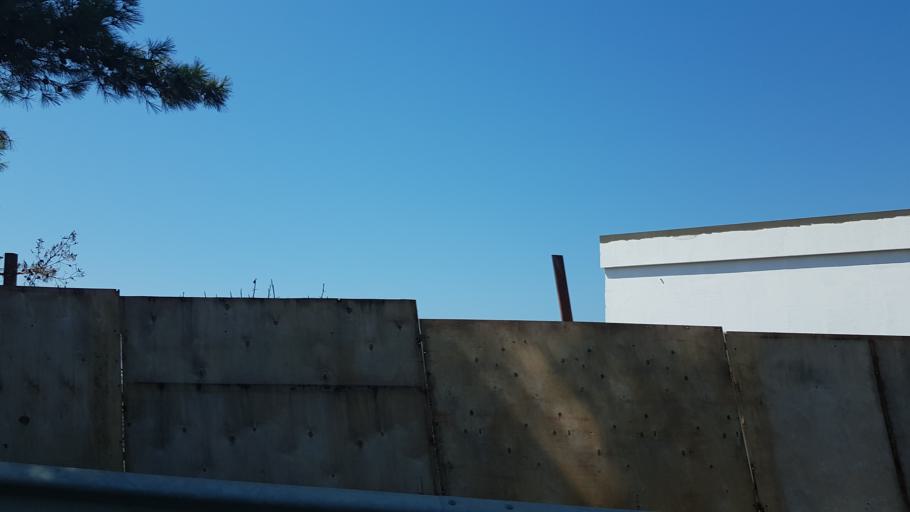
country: TR
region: Mugla
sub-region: Bodrum
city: Bodrum
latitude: 37.1031
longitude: 27.5027
